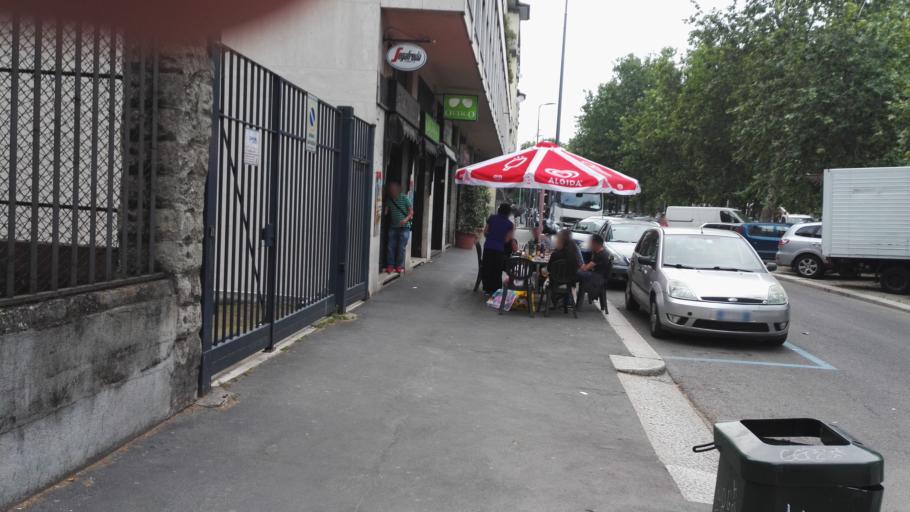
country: IT
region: Lombardy
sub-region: Citta metropolitana di Milano
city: Milano
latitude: 45.4548
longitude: 9.2239
